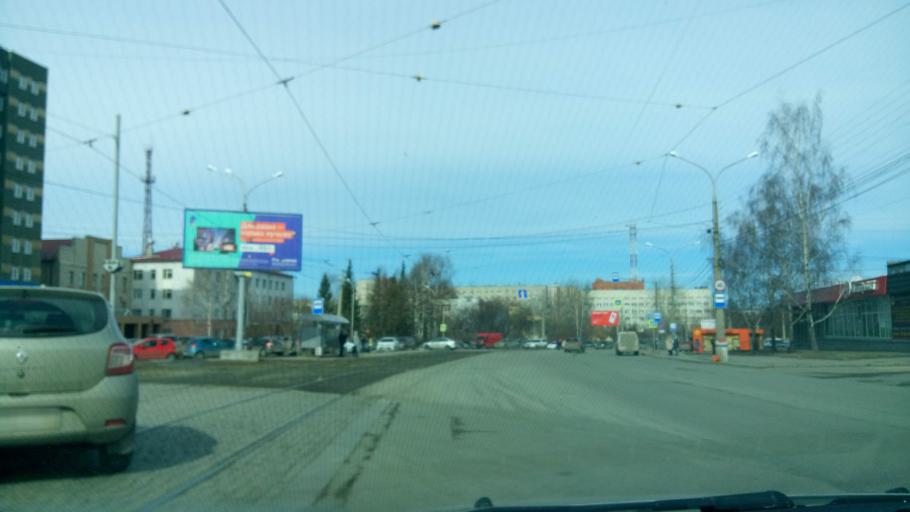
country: RU
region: Sverdlovsk
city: Nizhniy Tagil
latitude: 57.9087
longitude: 59.9473
